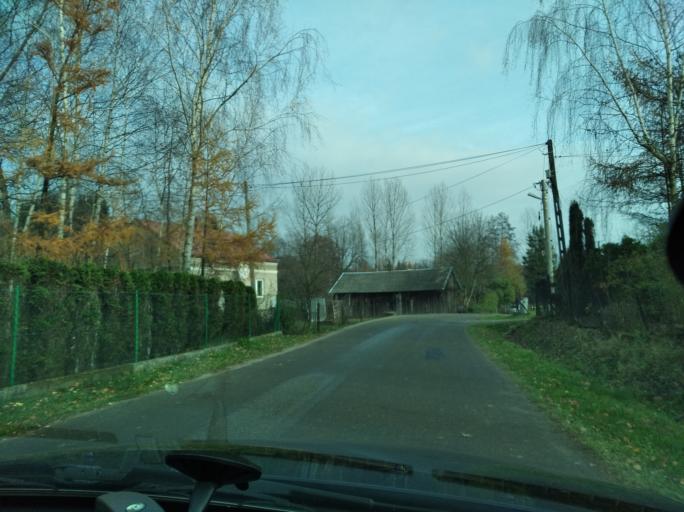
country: PL
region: Subcarpathian Voivodeship
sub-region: Powiat przeworski
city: Siedleczka
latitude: 49.9661
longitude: 22.3661
